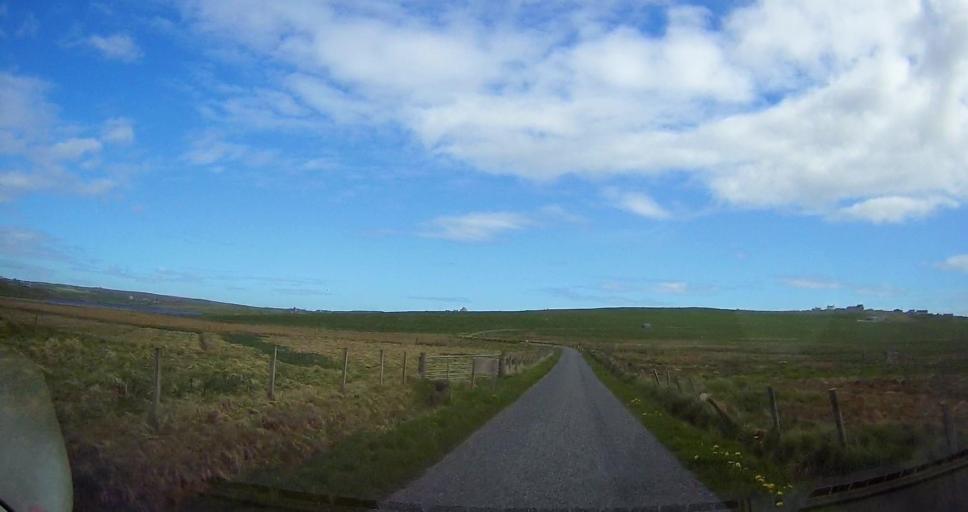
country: GB
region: Scotland
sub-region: Shetland Islands
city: Sandwick
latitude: 59.9228
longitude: -1.3281
